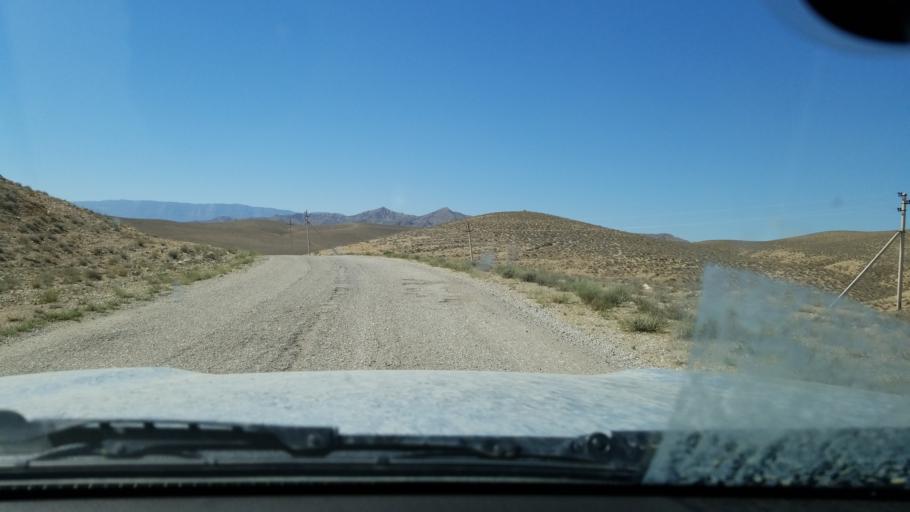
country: TM
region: Balkan
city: Balkanabat
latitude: 39.9095
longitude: 54.4295
